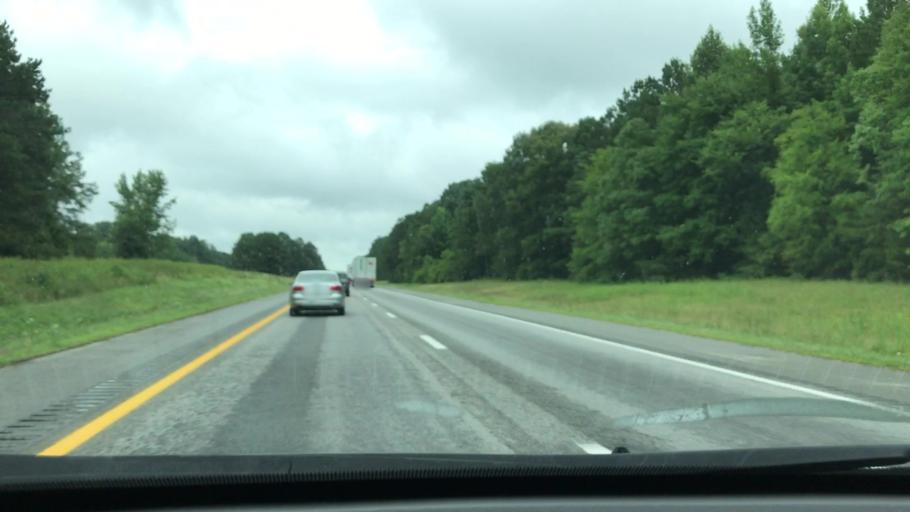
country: US
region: Virginia
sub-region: City of Emporia
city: Emporia
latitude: 36.7766
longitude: -77.4621
